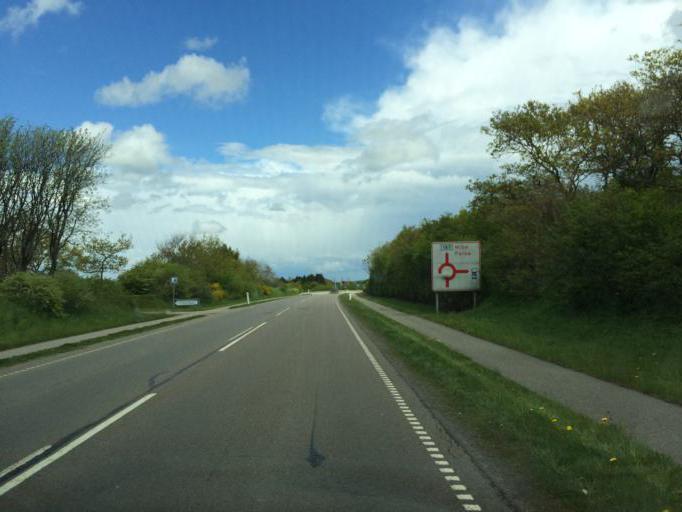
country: DK
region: North Denmark
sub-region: Vesthimmerland Kommune
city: Farso
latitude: 56.7577
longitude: 9.3311
